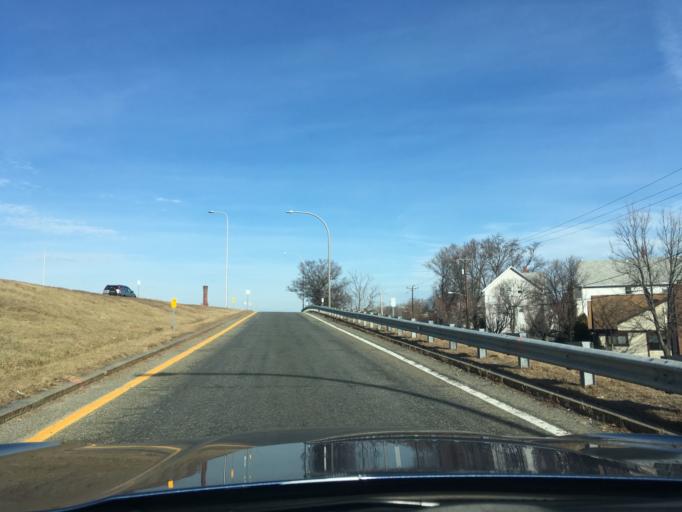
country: US
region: Rhode Island
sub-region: Providence County
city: Pawtucket
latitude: 41.8914
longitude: -71.3782
